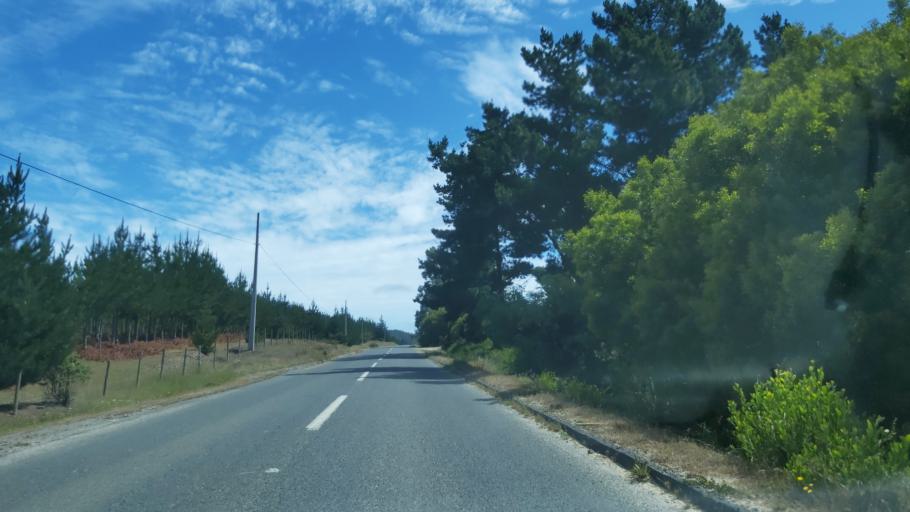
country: CL
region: Maule
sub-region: Provincia de Talca
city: Constitucion
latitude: -35.5553
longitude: -72.5825
